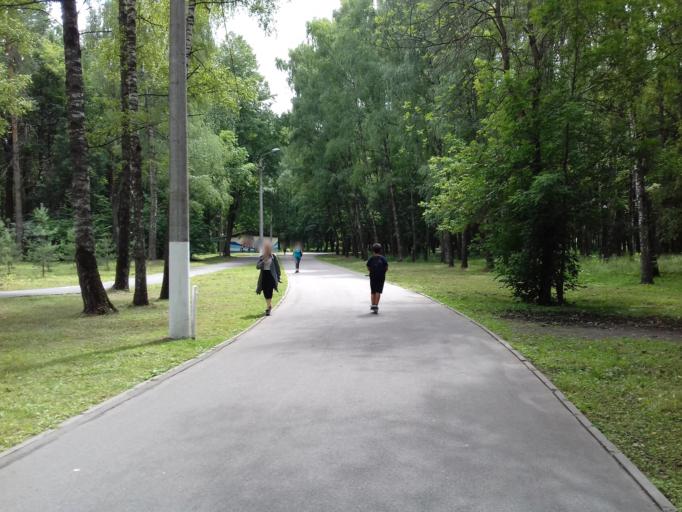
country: RU
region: Tula
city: Tula
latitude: 54.1851
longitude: 37.5844
